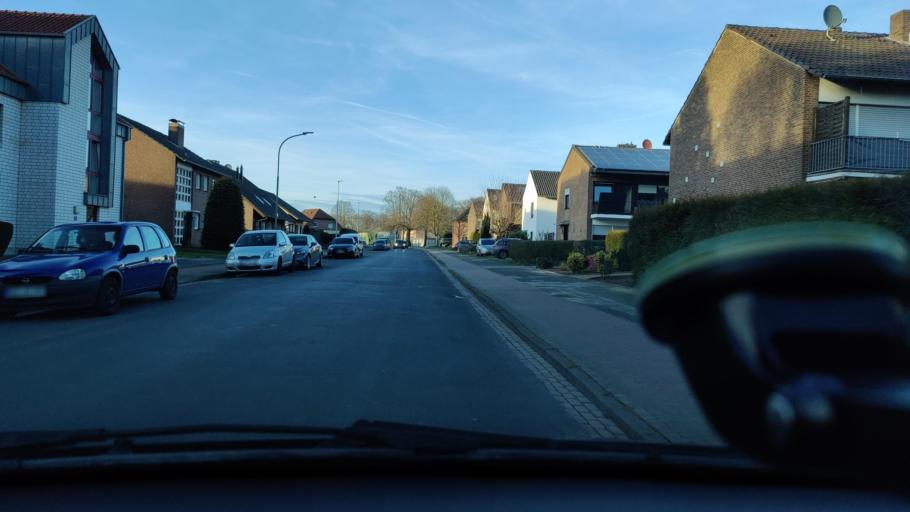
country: DE
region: North Rhine-Westphalia
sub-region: Regierungsbezirk Dusseldorf
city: Goch
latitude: 51.6821
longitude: 6.1693
